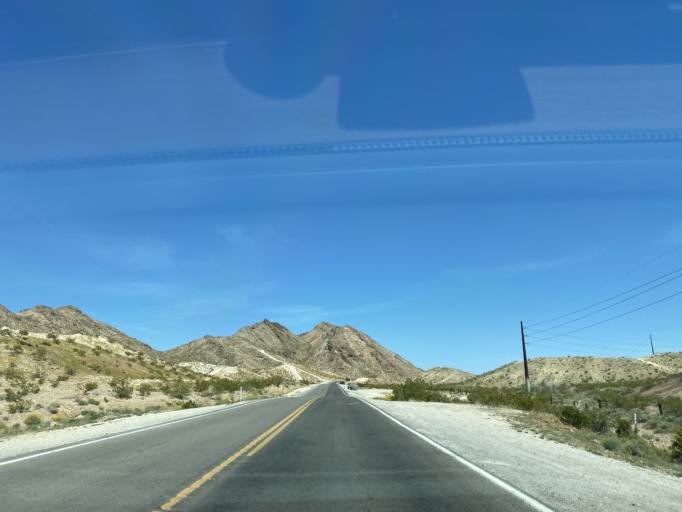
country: US
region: Nevada
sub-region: Clark County
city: Nellis Air Force Base
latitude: 36.2011
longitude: -114.9932
